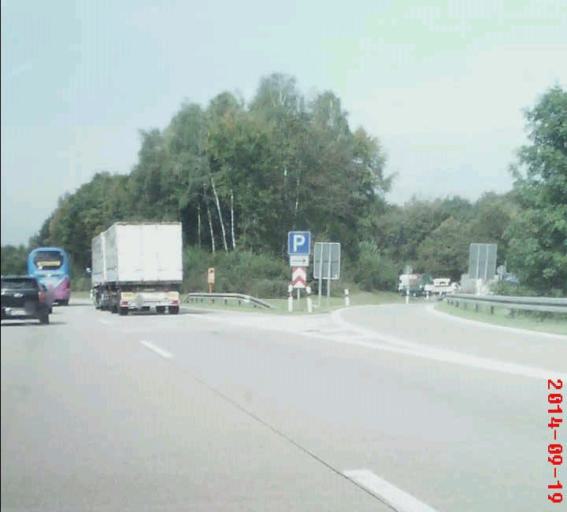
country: DE
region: Bavaria
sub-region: Lower Bavaria
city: Iggensbach
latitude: 48.7170
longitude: 13.1587
